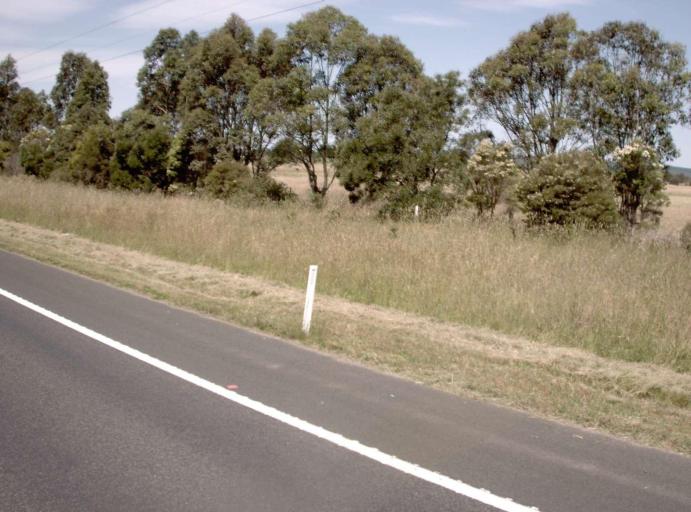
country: AU
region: Victoria
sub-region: Wellington
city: Heyfield
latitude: -38.1579
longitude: 146.7433
